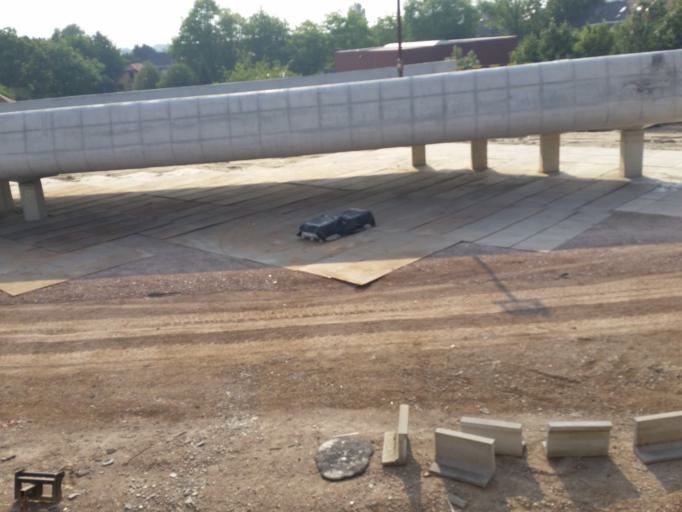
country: BE
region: Flanders
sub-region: Provincie Antwerpen
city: Mechelen
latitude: 51.0102
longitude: 4.4758
